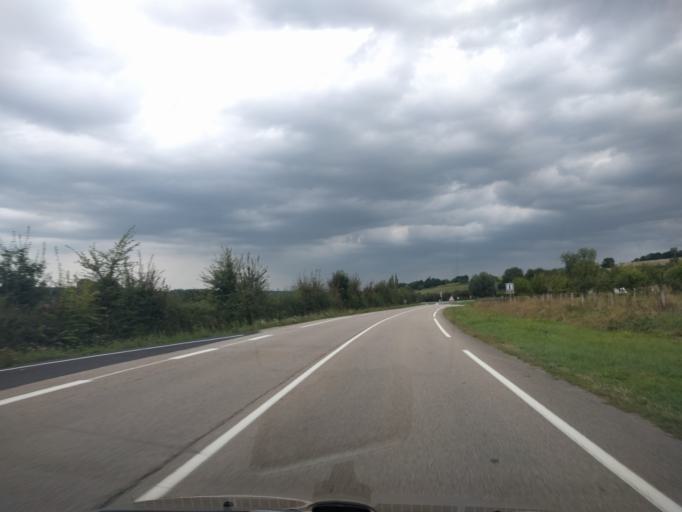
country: FR
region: Lower Normandy
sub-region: Departement de l'Orne
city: Gace
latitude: 48.7758
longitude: 0.3026
